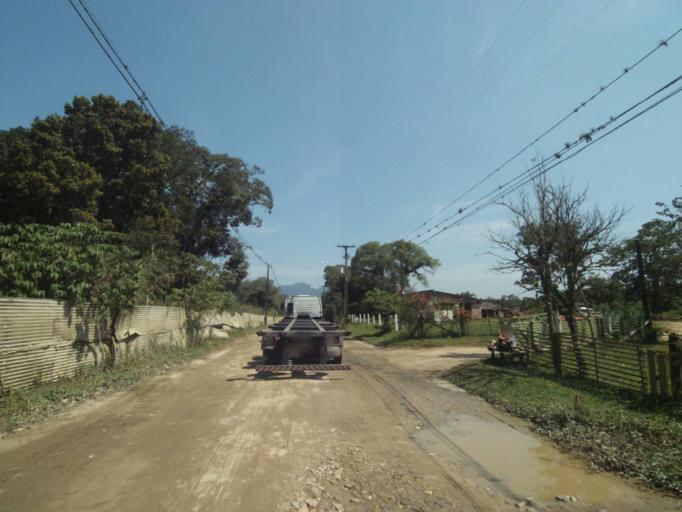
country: BR
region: Parana
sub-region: Paranagua
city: Paranagua
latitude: -25.5539
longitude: -48.5917
